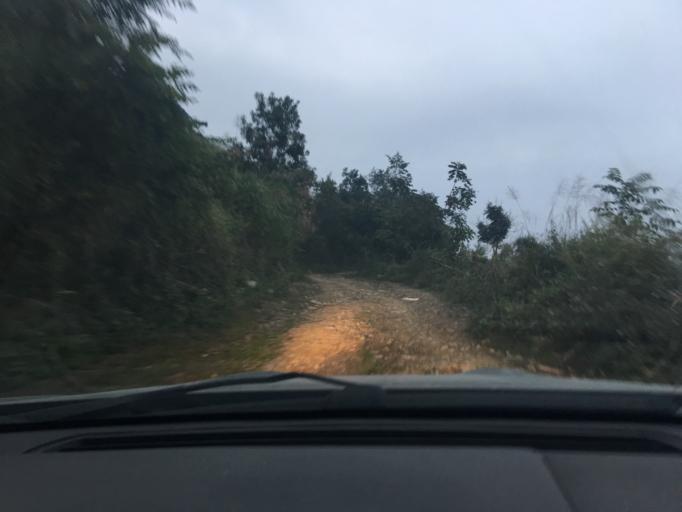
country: CN
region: Guangxi Zhuangzu Zizhiqu
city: Xinzhou
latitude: 24.9032
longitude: 105.5919
